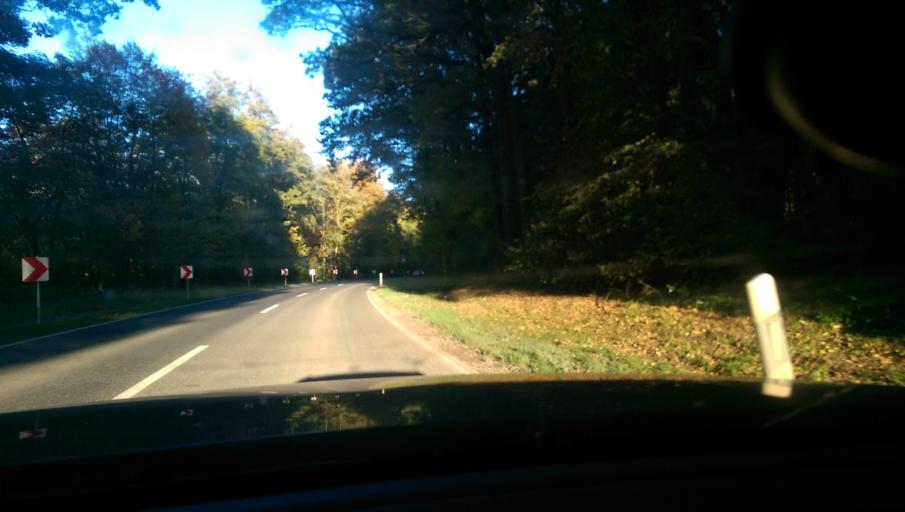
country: DE
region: Bavaria
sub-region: Regierungsbezirk Unterfranken
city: Schwebheim
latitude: 50.0138
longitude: 10.2317
